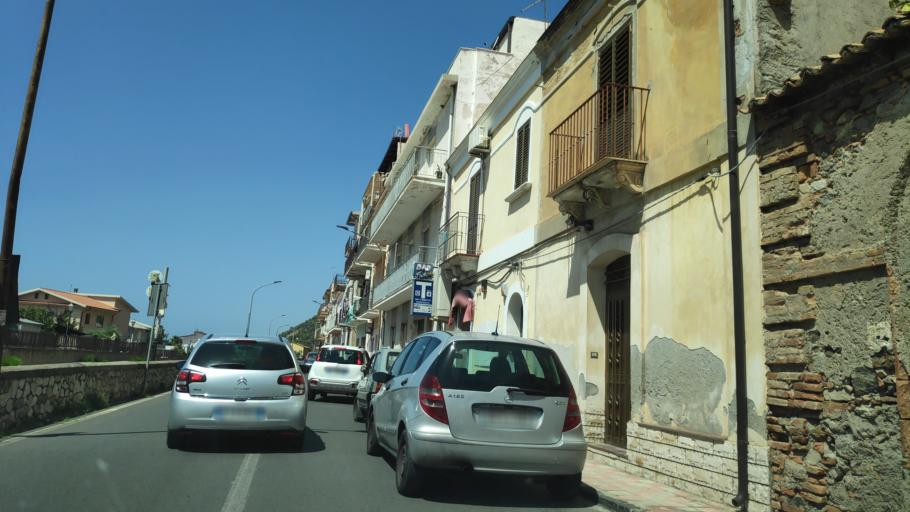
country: IT
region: Calabria
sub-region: Provincia di Reggio Calabria
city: Palizzi Marina
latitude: 37.9194
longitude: 15.9794
